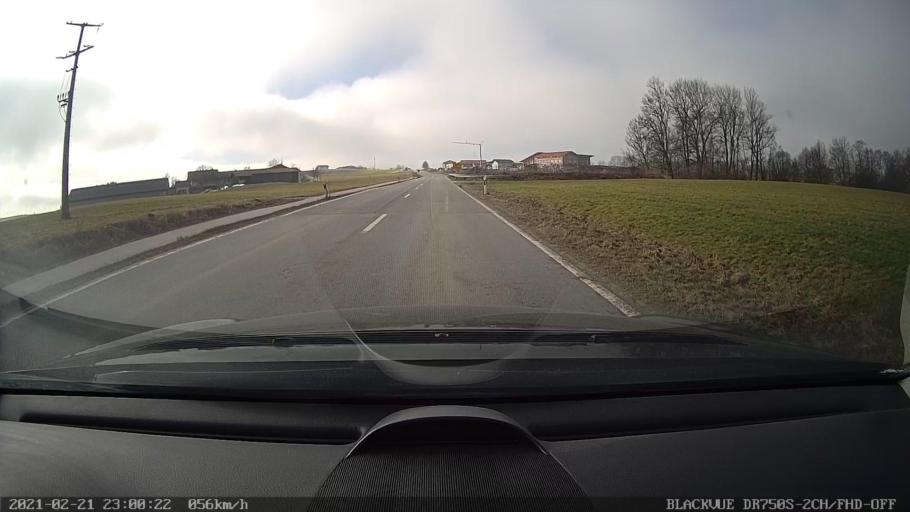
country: DE
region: Bavaria
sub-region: Upper Bavaria
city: Griesstatt
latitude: 48.0032
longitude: 12.1816
